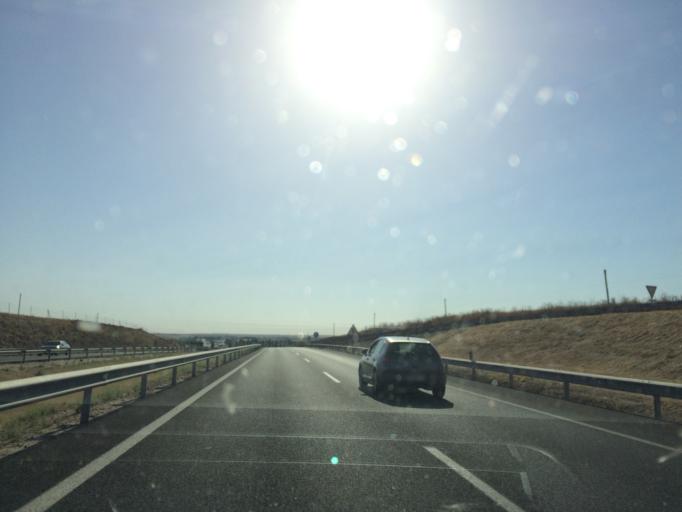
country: ES
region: Castille-La Mancha
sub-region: Province of Toledo
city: Otero
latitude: 40.0168
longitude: -4.5424
